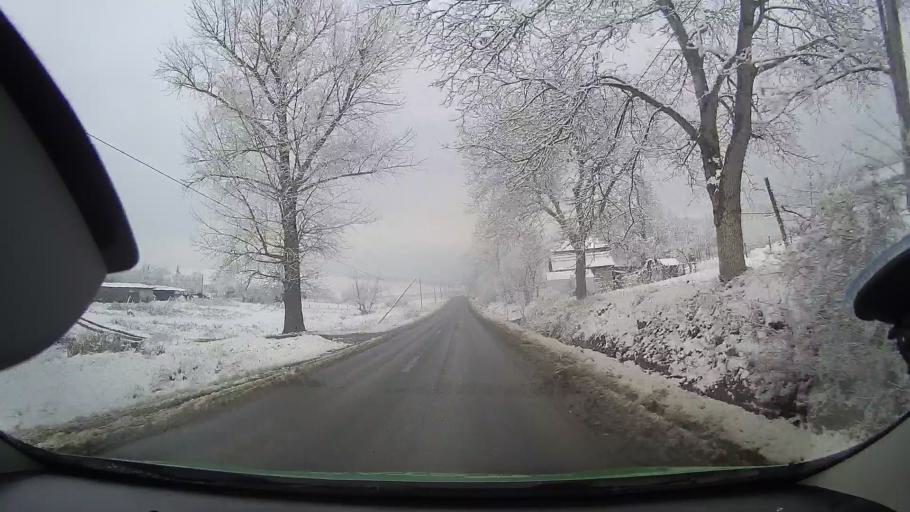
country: RO
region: Mures
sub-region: Comuna Atintis
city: Atintis
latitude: 46.4475
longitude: 24.0878
